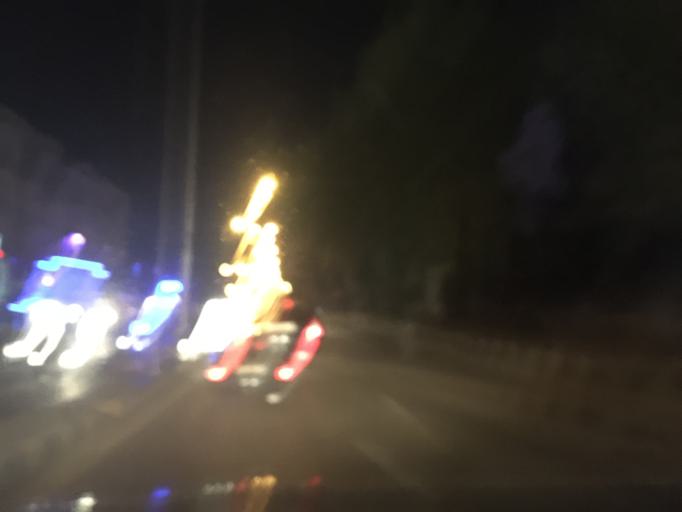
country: JO
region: Amman
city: Amman
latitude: 31.9979
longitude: 35.9315
